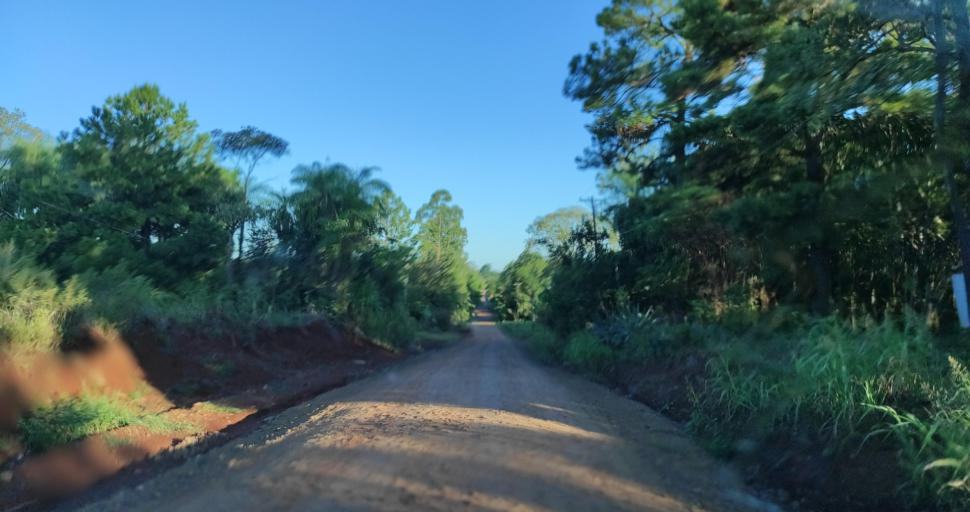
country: AR
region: Misiones
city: Gobernador Roca
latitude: -27.1977
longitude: -55.4641
